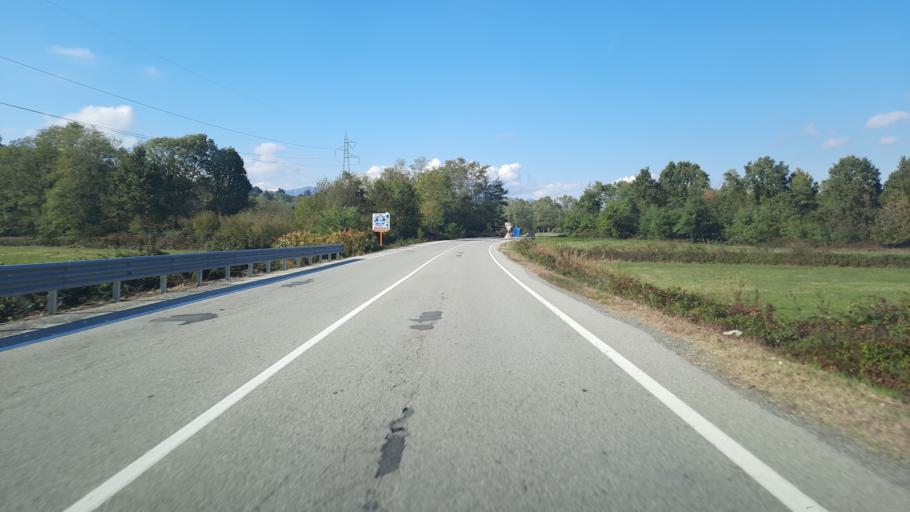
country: IT
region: Piedmont
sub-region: Provincia di Novara
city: Gargallo
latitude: 45.7259
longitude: 8.4381
